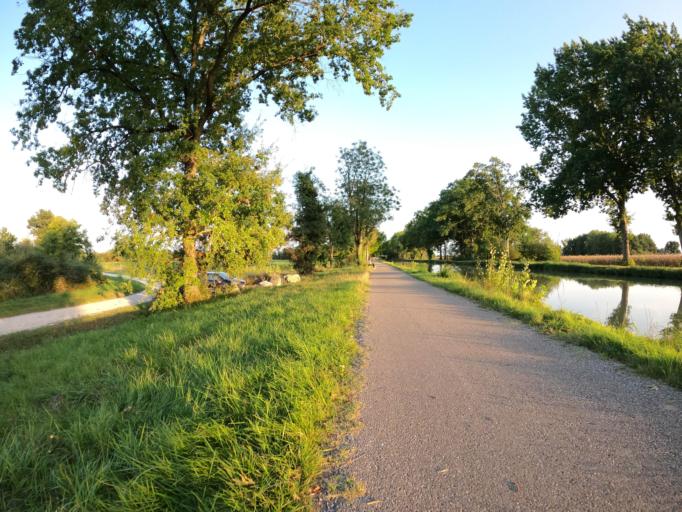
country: FR
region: Midi-Pyrenees
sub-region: Departement du Tarn-et-Garonne
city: Saint-Porquier
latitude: 43.9852
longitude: 1.2091
